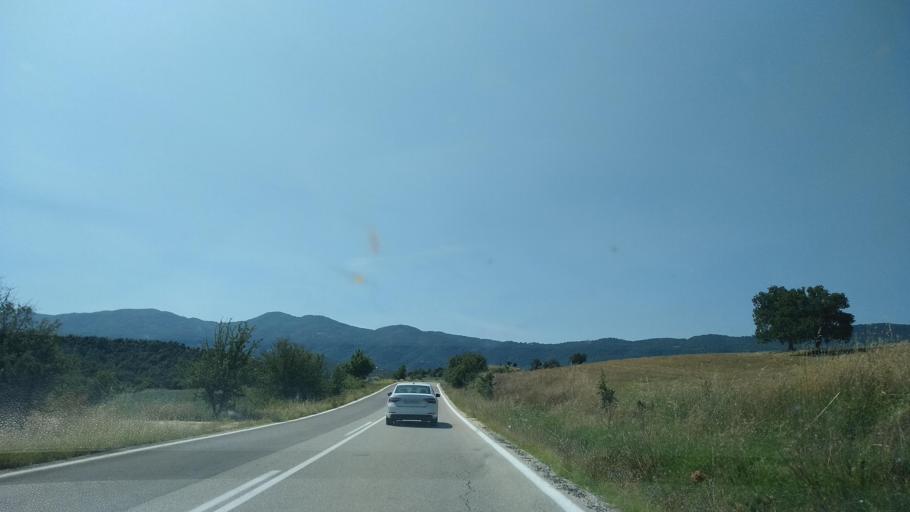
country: GR
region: Central Macedonia
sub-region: Nomos Thessalonikis
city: Nea Apollonia
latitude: 40.5213
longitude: 23.4720
